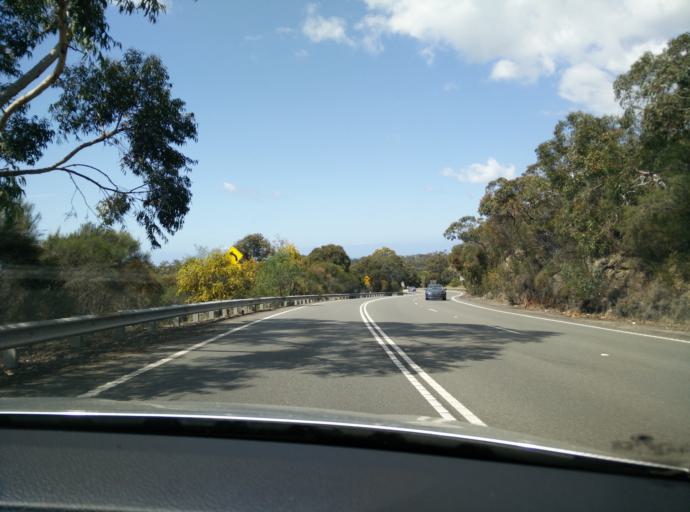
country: AU
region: New South Wales
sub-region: Gosford Shire
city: Blackwall
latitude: -33.4774
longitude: 151.2911
